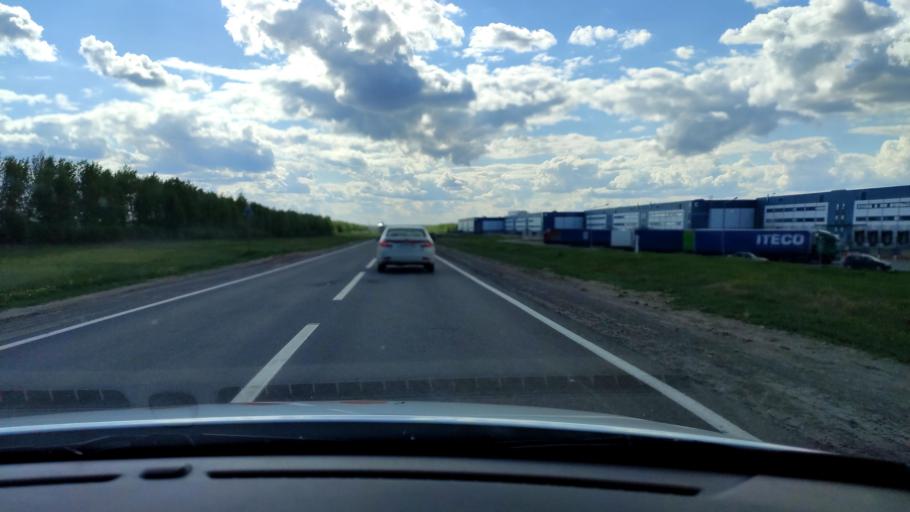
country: RU
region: Tatarstan
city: Stolbishchi
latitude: 55.6337
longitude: 49.2619
